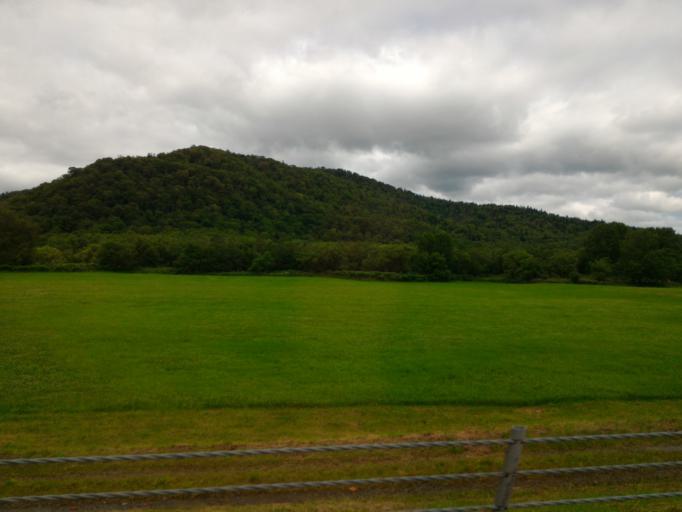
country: JP
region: Hokkaido
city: Nayoro
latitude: 44.7233
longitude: 142.2502
